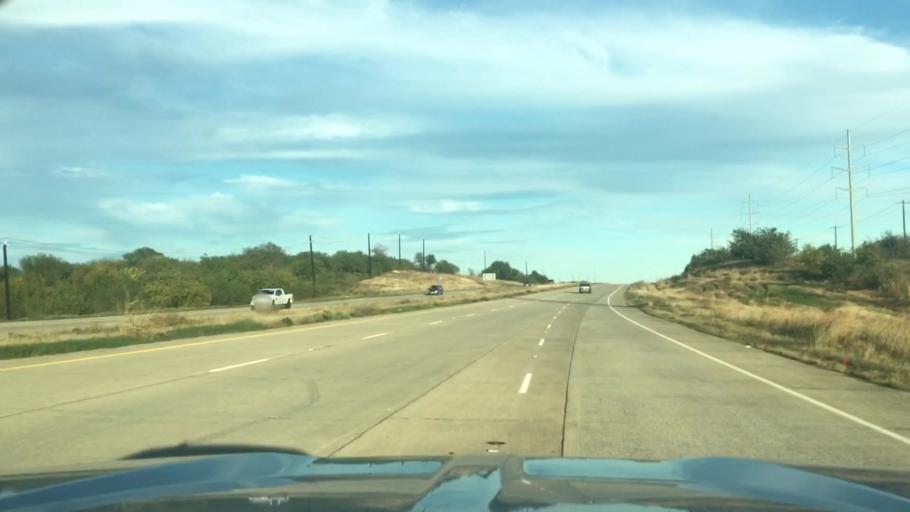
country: US
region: Texas
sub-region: Denton County
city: Denton
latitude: 33.2578
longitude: -97.1604
